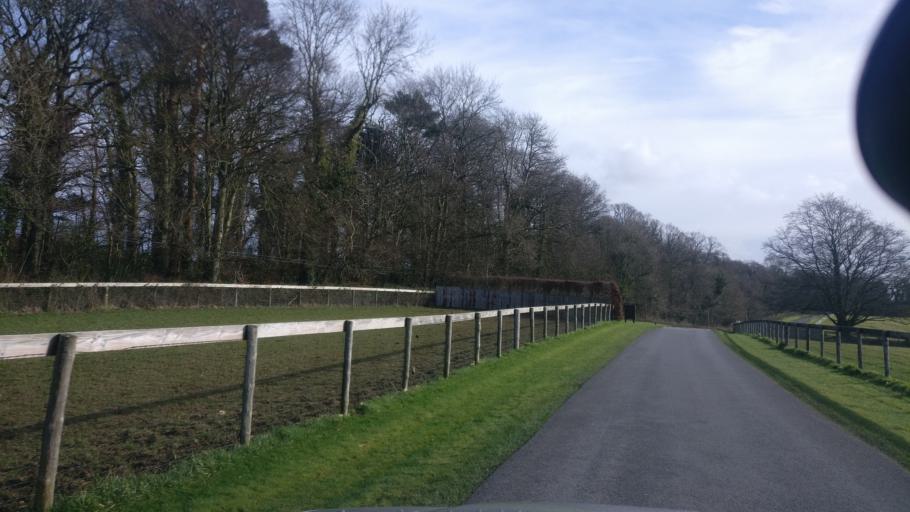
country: IE
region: Leinster
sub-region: Kilkenny
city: Thomastown
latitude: 52.5318
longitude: -7.1735
